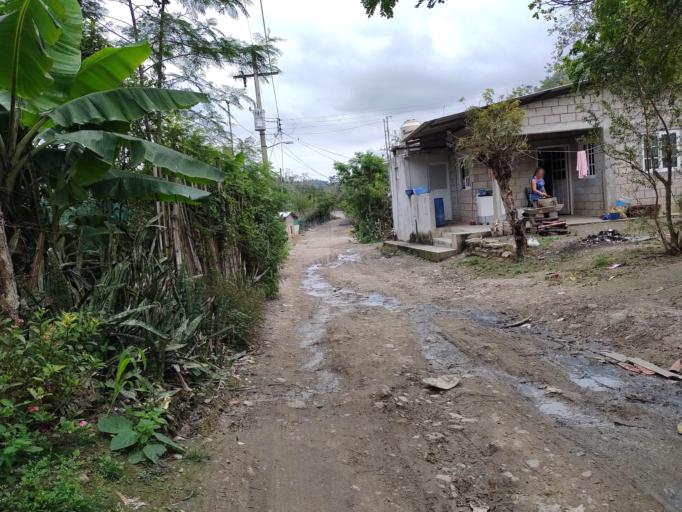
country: MX
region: Veracruz
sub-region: Papantla
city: Polutla
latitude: 20.4665
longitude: -97.2575
